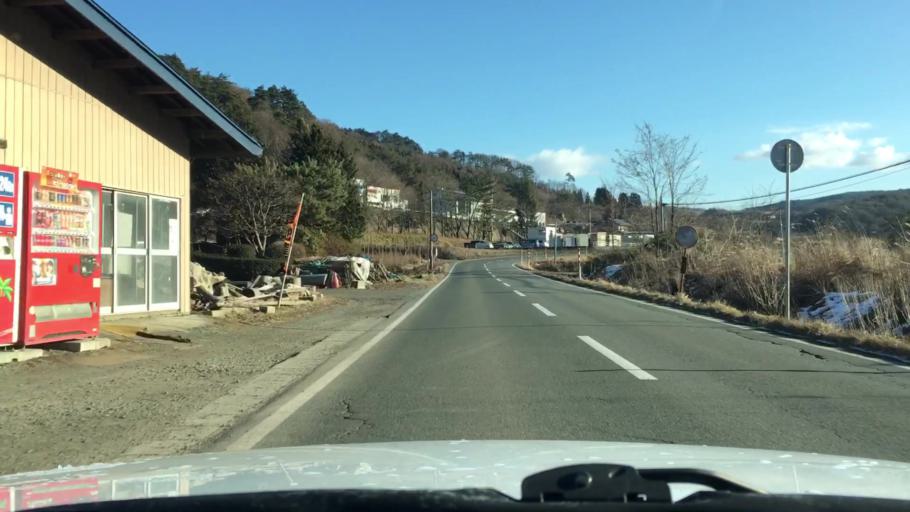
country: JP
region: Iwate
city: Morioka-shi
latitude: 39.6610
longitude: 141.1951
